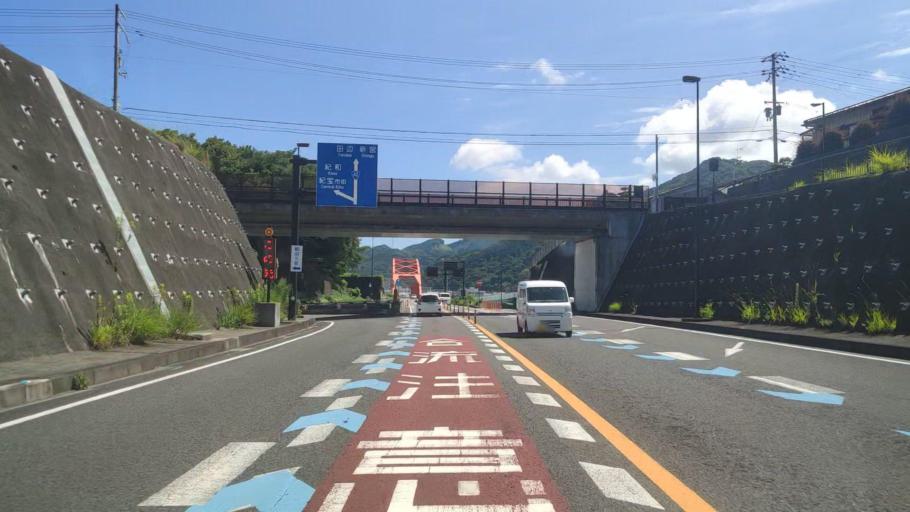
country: JP
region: Wakayama
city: Shingu
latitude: 33.7362
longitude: 135.9884
